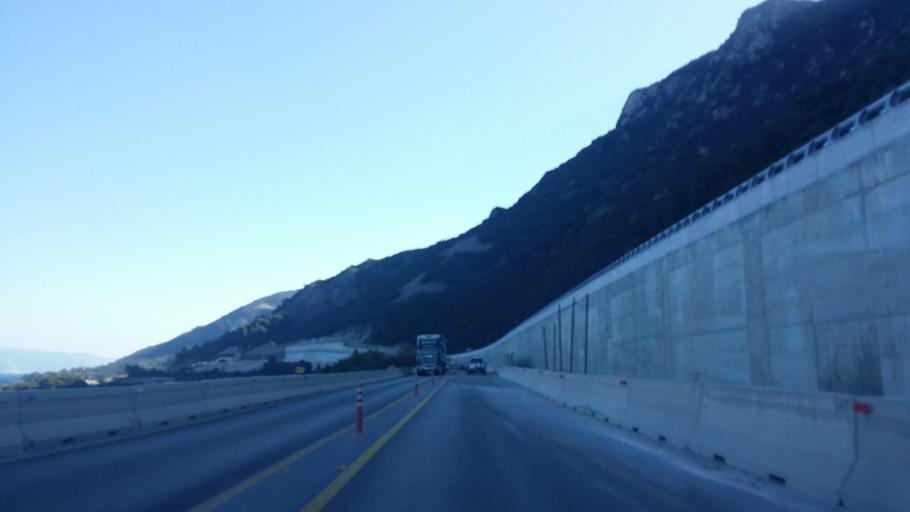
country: GR
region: West Greece
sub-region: Nomos Achaias
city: Ano Kastritsion
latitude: 38.3239
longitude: 21.9008
